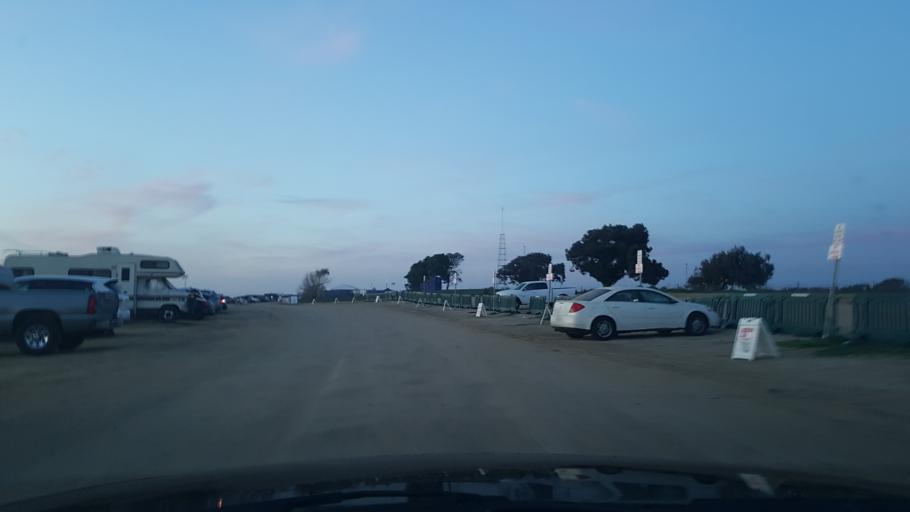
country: US
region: California
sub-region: San Diego County
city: La Jolla
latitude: 32.8905
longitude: -117.2494
